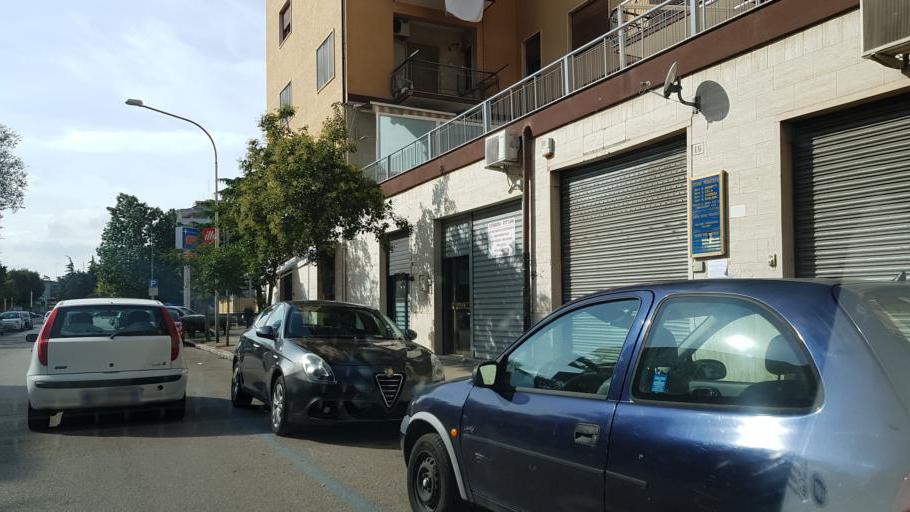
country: IT
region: Apulia
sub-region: Provincia di Foggia
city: Foggia
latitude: 41.4542
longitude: 15.5616
